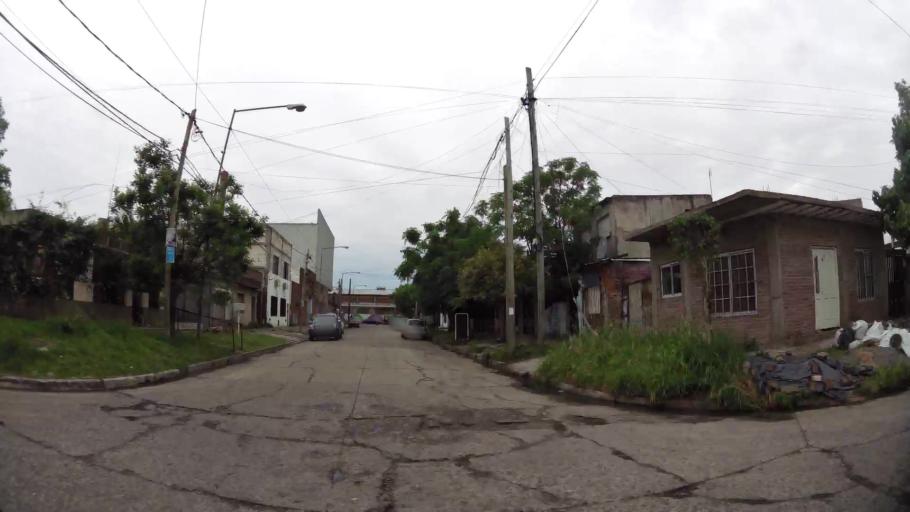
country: AR
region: Buenos Aires
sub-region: Partido de Lanus
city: Lanus
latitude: -34.7013
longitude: -58.3668
